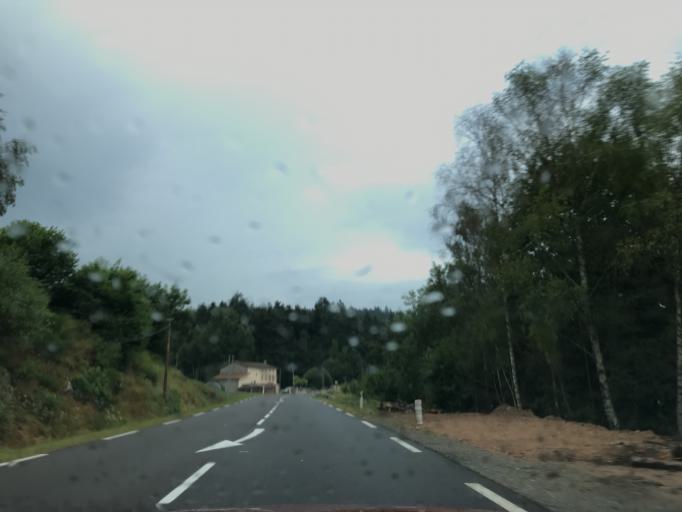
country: FR
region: Rhone-Alpes
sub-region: Departement de la Loire
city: Noiretable
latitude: 45.8424
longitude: 3.7438
